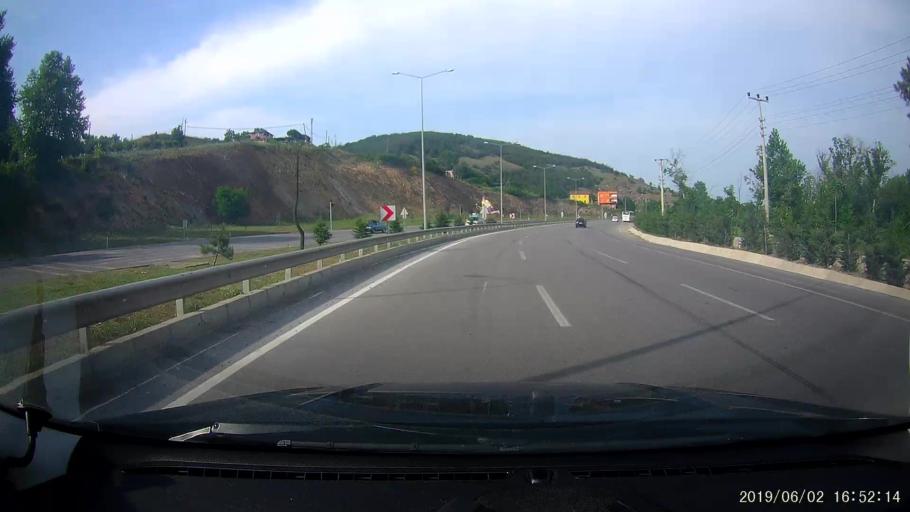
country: TR
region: Samsun
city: Samsun
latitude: 41.2851
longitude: 36.1936
